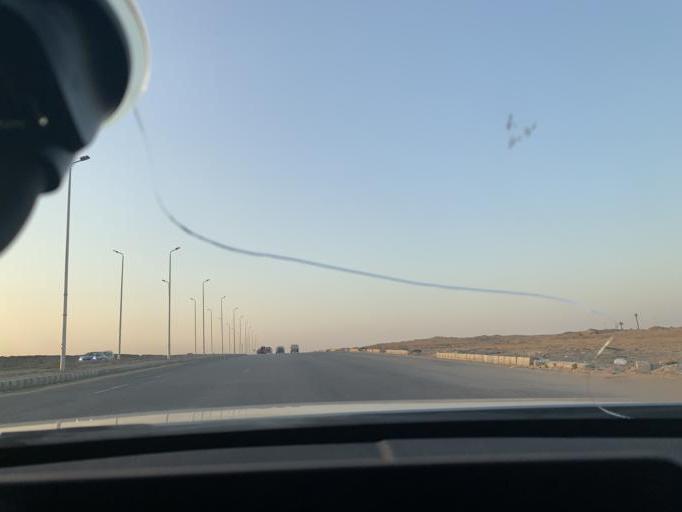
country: EG
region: Muhafazat al Qahirah
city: Halwan
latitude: 29.9856
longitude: 31.4688
